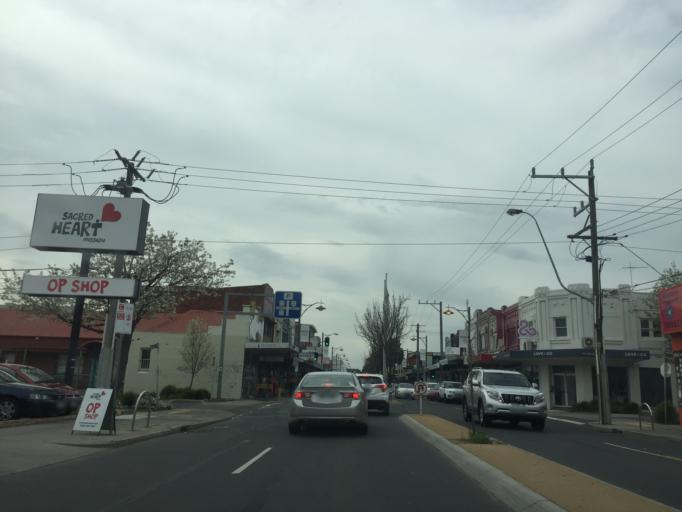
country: AU
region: Victoria
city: Thornbury
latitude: -37.7428
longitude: 145.0032
